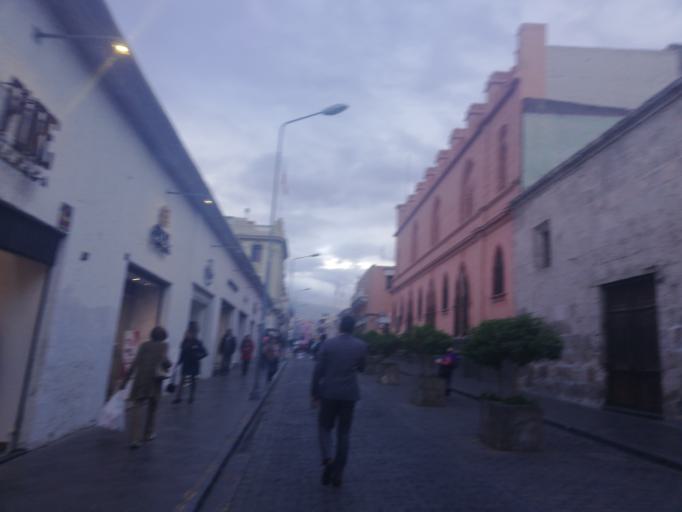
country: PE
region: Arequipa
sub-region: Provincia de Arequipa
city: Arequipa
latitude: -16.3979
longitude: -71.5360
